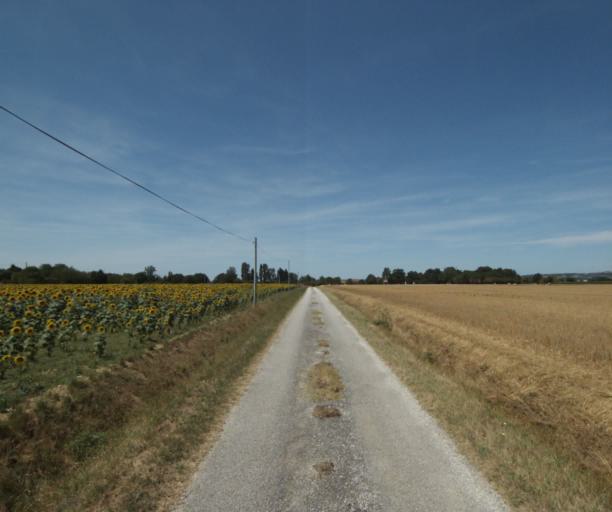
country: FR
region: Midi-Pyrenees
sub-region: Departement de la Haute-Garonne
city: Revel
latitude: 43.5003
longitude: 2.0275
